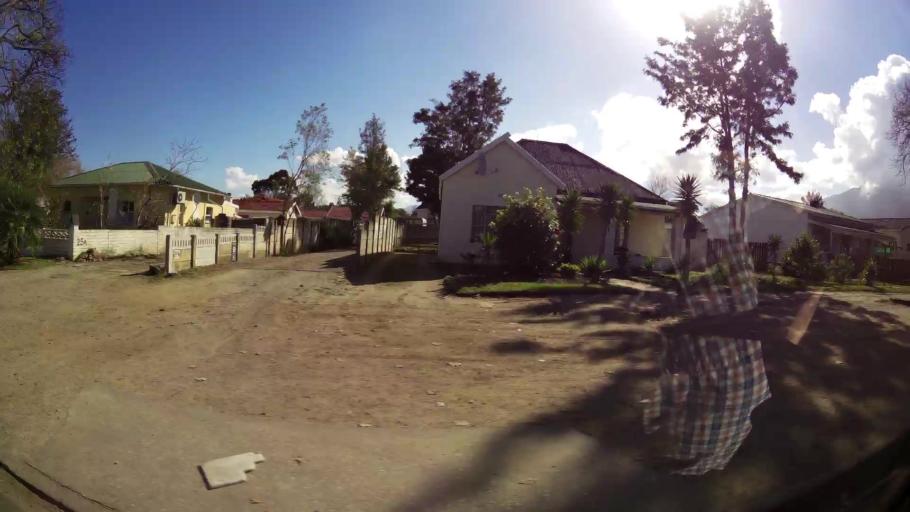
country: ZA
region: Western Cape
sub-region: Eden District Municipality
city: George
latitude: -33.9694
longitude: 22.4527
